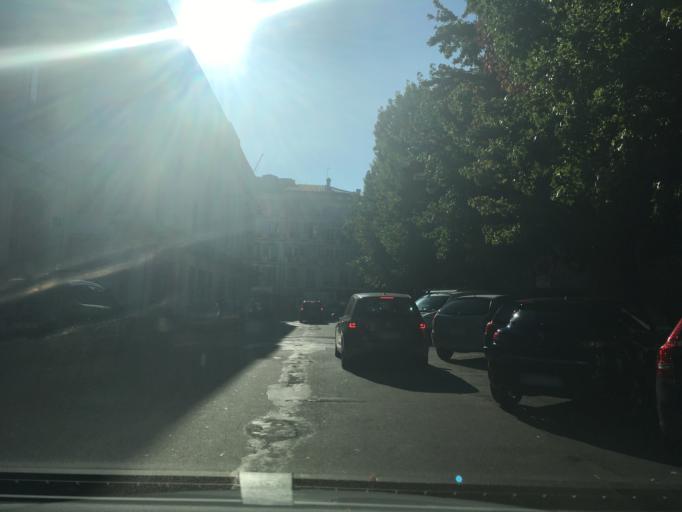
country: FR
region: Aquitaine
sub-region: Departement des Pyrenees-Atlantiques
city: Bayonne
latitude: 43.4924
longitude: -1.4780
